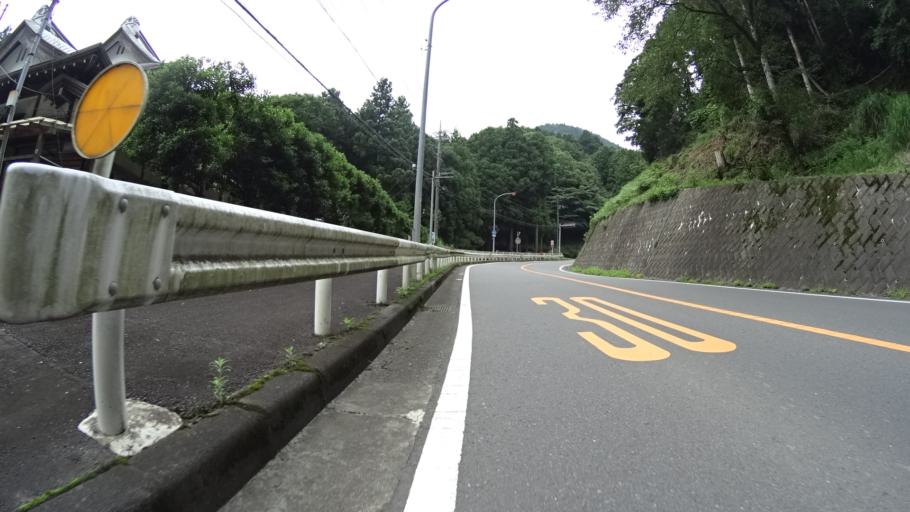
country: JP
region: Kanagawa
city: Atsugi
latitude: 35.4961
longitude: 139.2650
